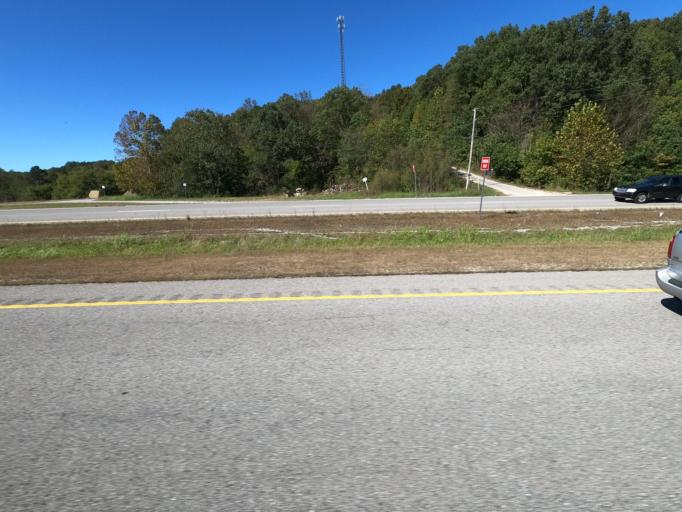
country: US
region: Tennessee
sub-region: Maury County
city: Mount Pleasant
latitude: 35.4817
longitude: -87.2558
